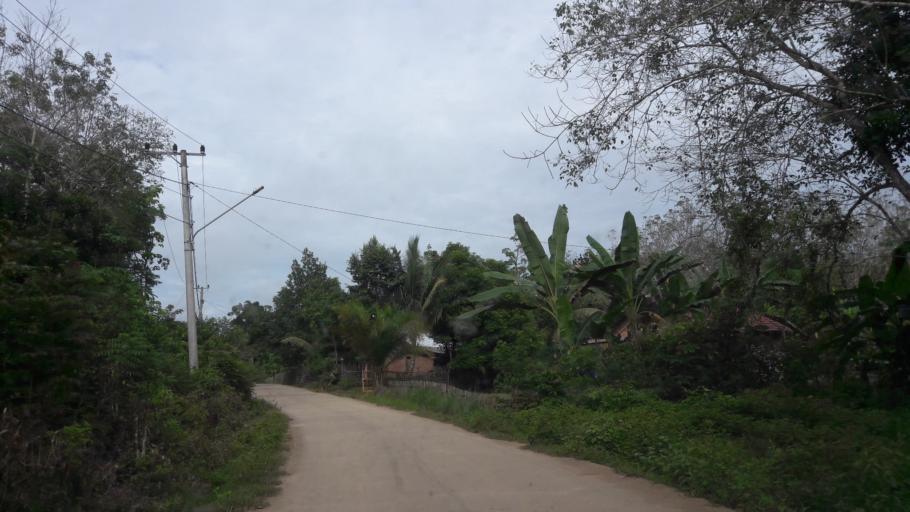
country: ID
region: South Sumatra
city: Gunungmegang Dalam
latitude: -3.2946
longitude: 103.6764
